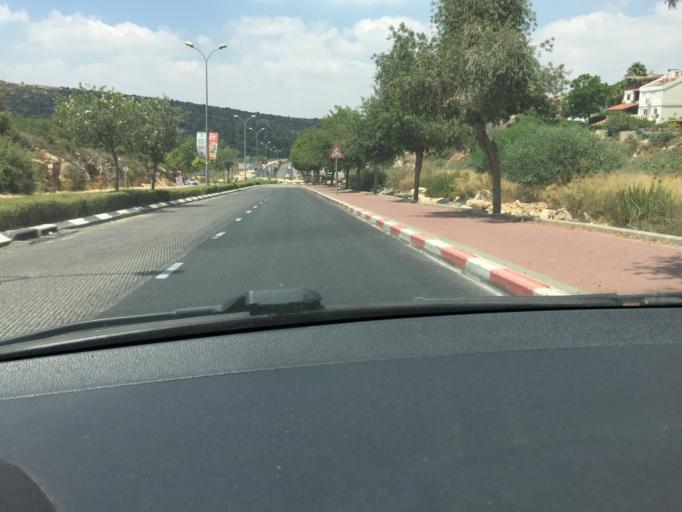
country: IL
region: Jerusalem
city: Ariel
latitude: 32.1022
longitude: 35.1752
